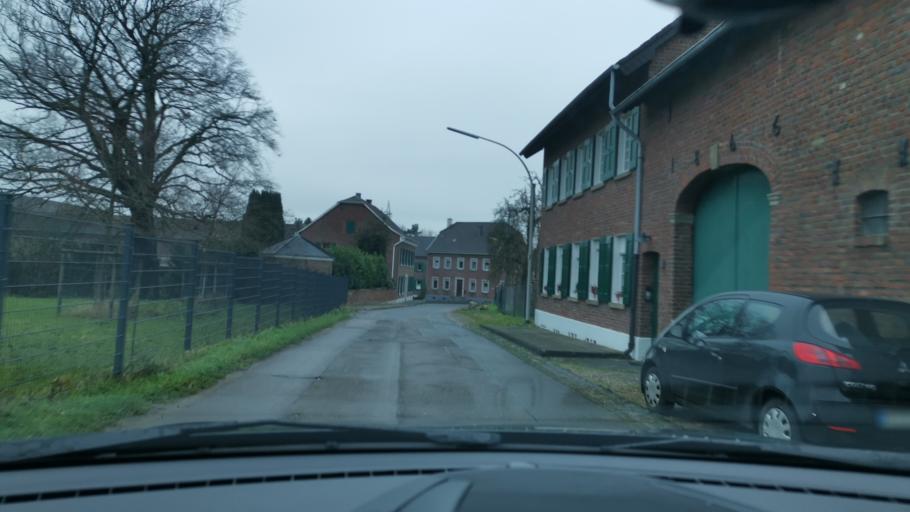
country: DE
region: North Rhine-Westphalia
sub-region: Regierungsbezirk Dusseldorf
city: Juchen
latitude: 51.1065
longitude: 6.5224
